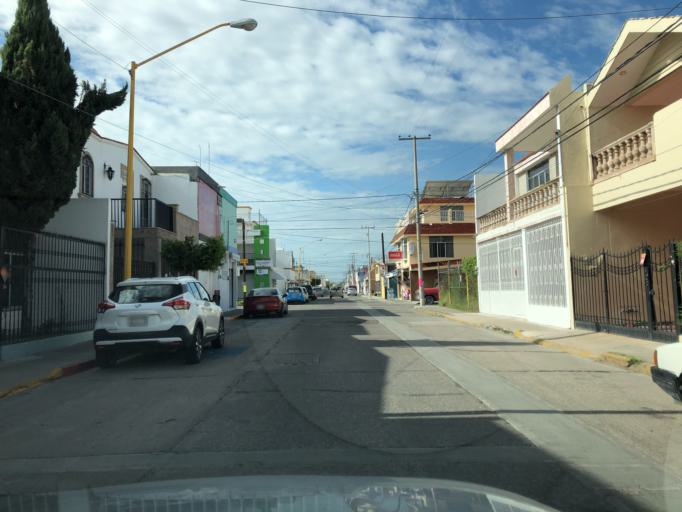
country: MX
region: Aguascalientes
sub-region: Aguascalientes
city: Aguascalientes
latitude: 21.8700
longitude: -102.3047
